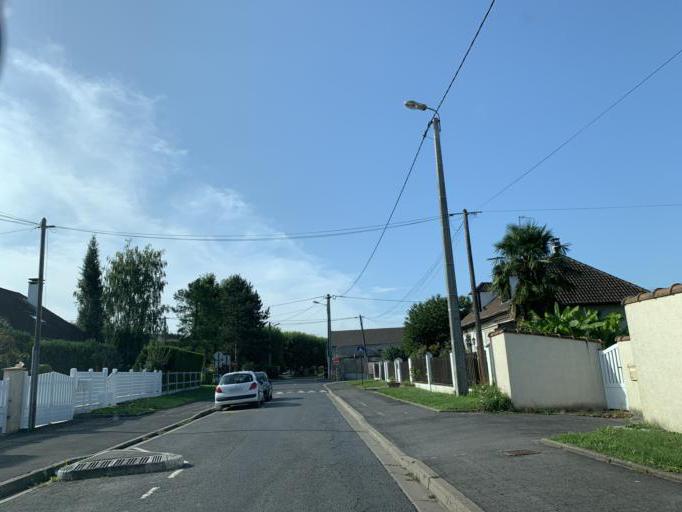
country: FR
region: Ile-de-France
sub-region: Departement de Seine-et-Marne
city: Claye-Souilly
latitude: 48.9411
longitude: 2.6949
